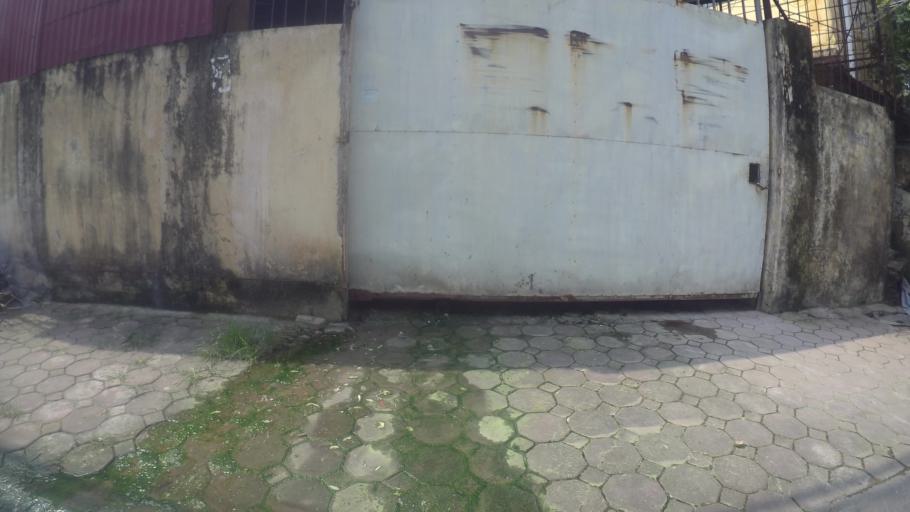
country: VN
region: Ha Noi
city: Tay Ho
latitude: 21.0875
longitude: 105.8123
